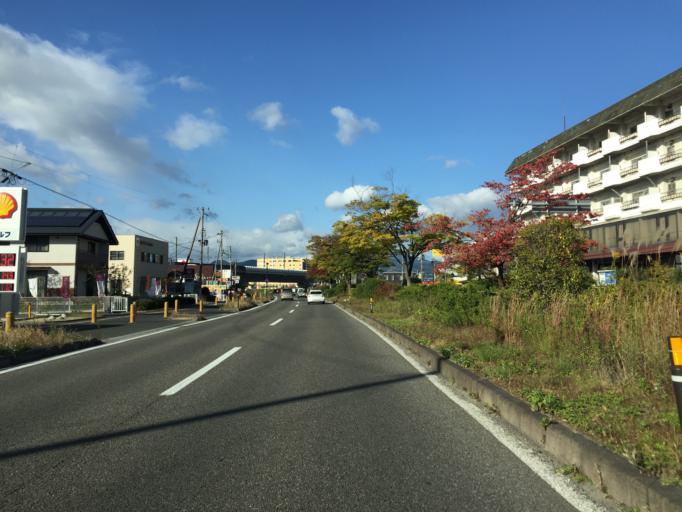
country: JP
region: Fukushima
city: Fukushima-shi
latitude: 37.7766
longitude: 140.4653
